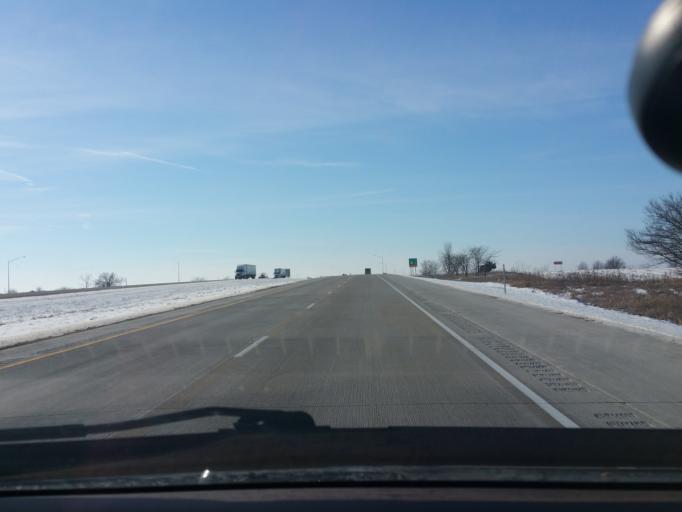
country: US
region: Iowa
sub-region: Decatur County
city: Lamoni
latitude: 40.5780
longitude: -93.9347
